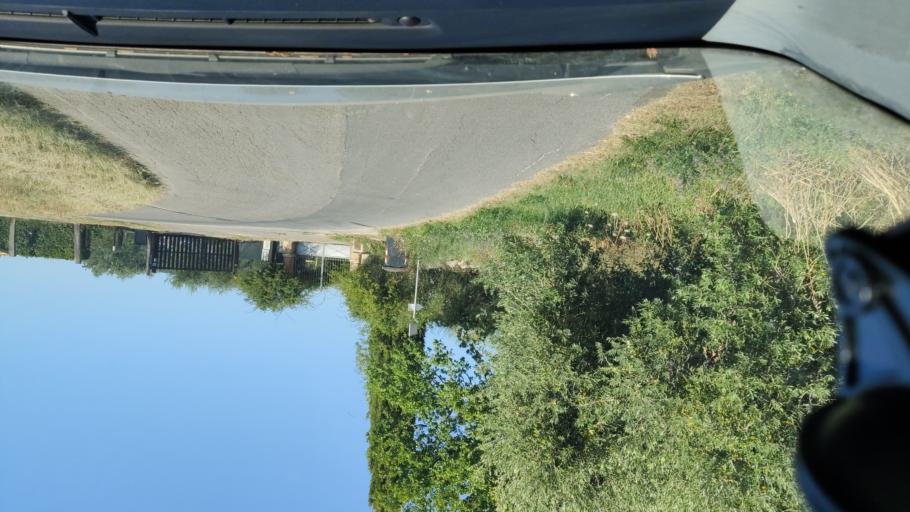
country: IT
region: Umbria
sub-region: Provincia di Terni
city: Amelia
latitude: 42.5385
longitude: 12.4306
